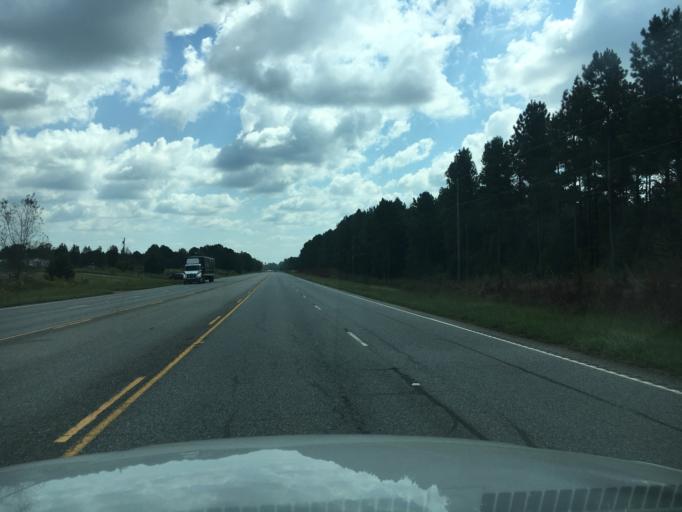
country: US
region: South Carolina
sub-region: Greenwood County
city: Ware Shoals
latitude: 34.4826
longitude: -82.2802
